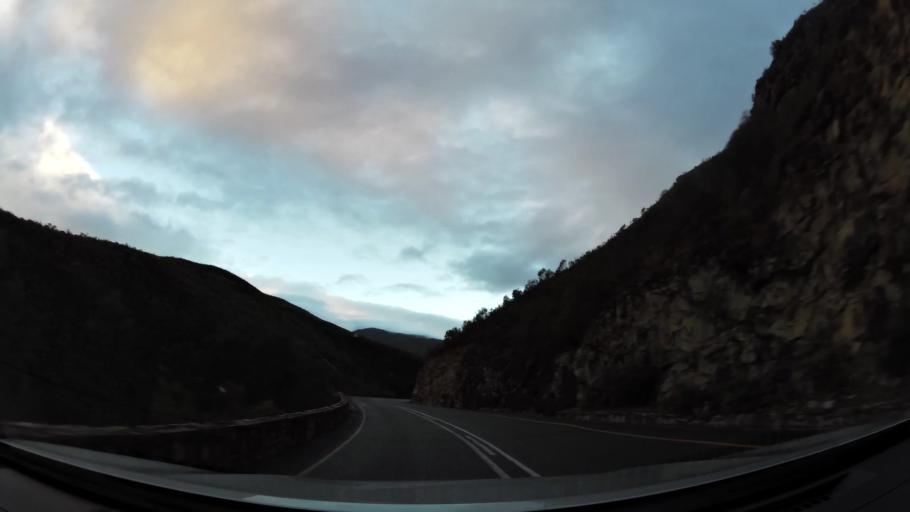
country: ZA
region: Western Cape
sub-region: Overberg District Municipality
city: Swellendam
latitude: -33.9897
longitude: 20.7098
